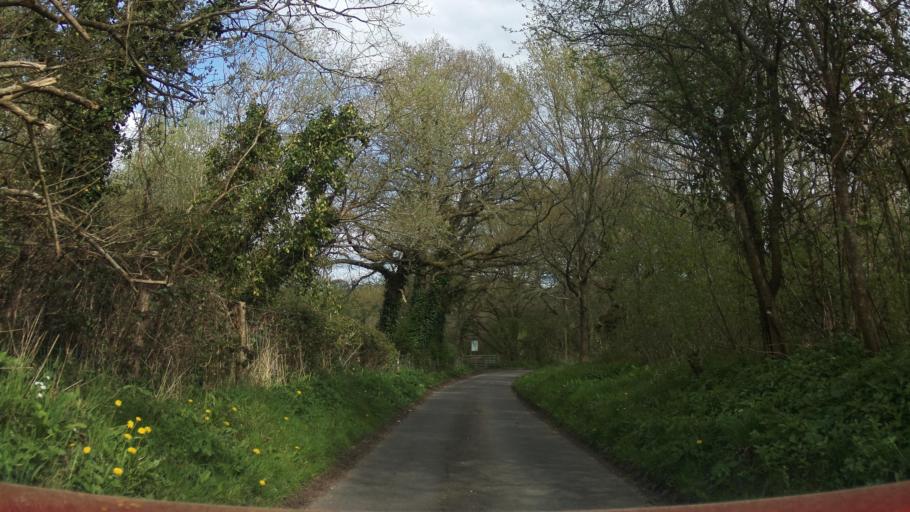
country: GB
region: England
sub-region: Hampshire
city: Romsey
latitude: 51.0273
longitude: -1.4959
